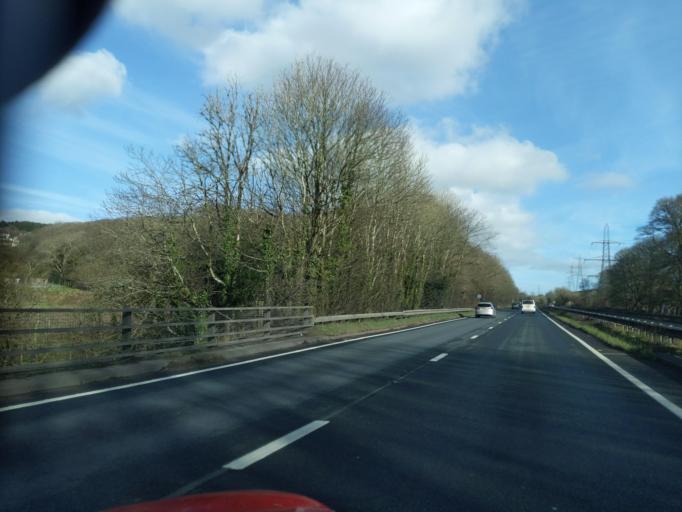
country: GB
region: England
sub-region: Devon
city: Ivybridge
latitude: 50.3930
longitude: -3.8789
